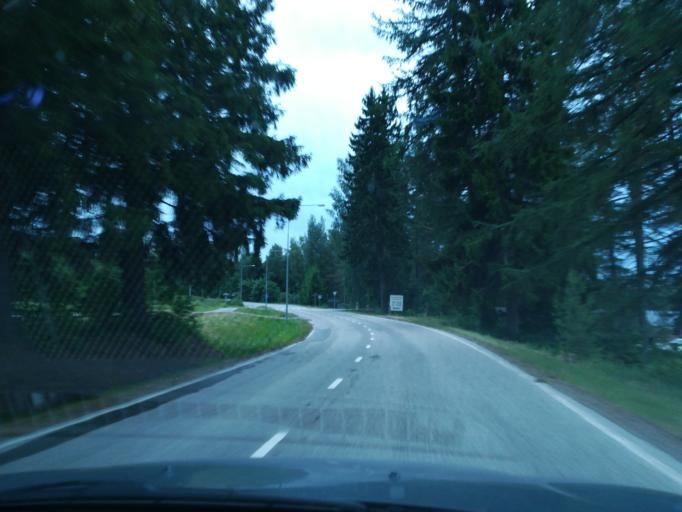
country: FI
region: Southern Savonia
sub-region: Mikkeli
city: Ristiina
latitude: 61.5024
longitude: 27.2652
